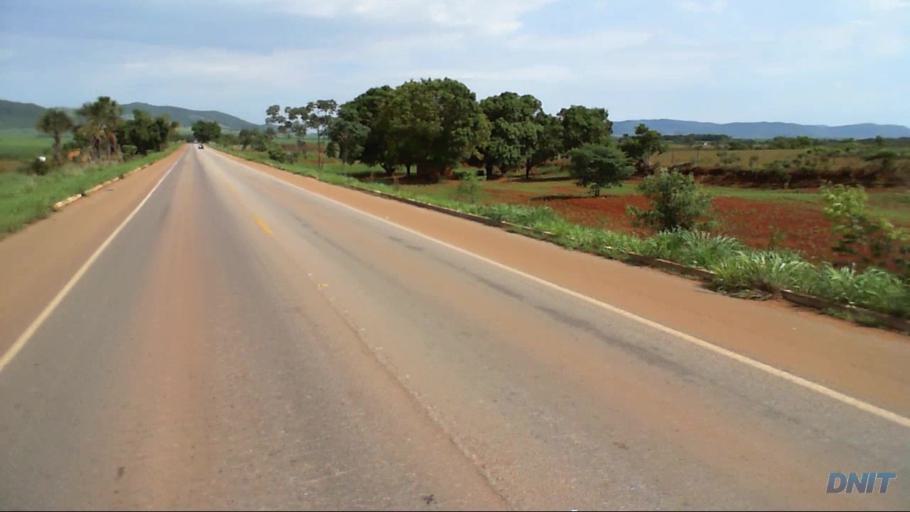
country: BR
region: Goias
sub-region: Barro Alto
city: Barro Alto
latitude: -15.0633
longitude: -48.8752
